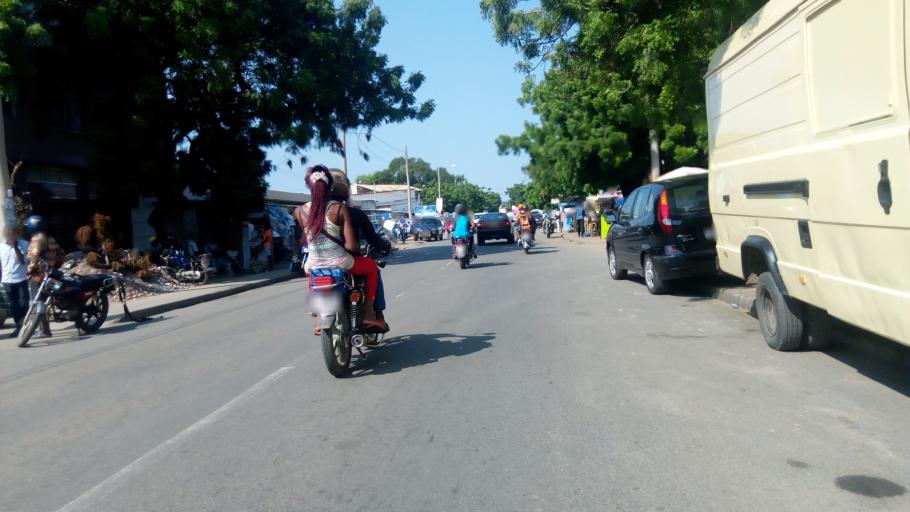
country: TG
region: Maritime
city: Lome
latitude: 6.1317
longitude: 1.2260
